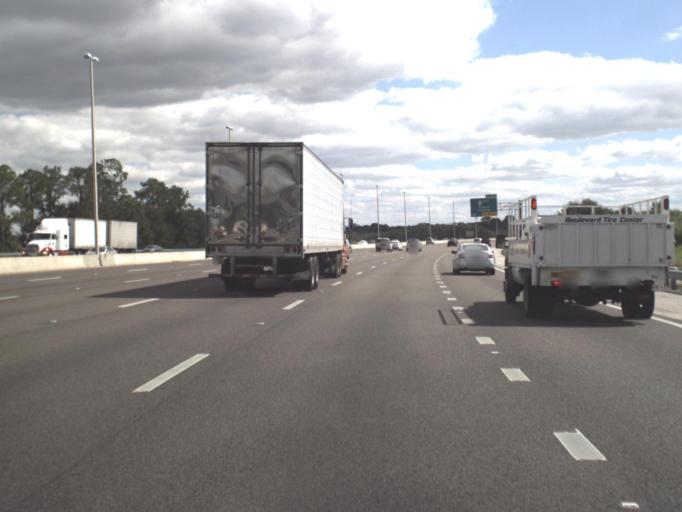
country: US
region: Florida
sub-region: Orange County
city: Ocoee
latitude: 28.5455
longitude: -81.5417
